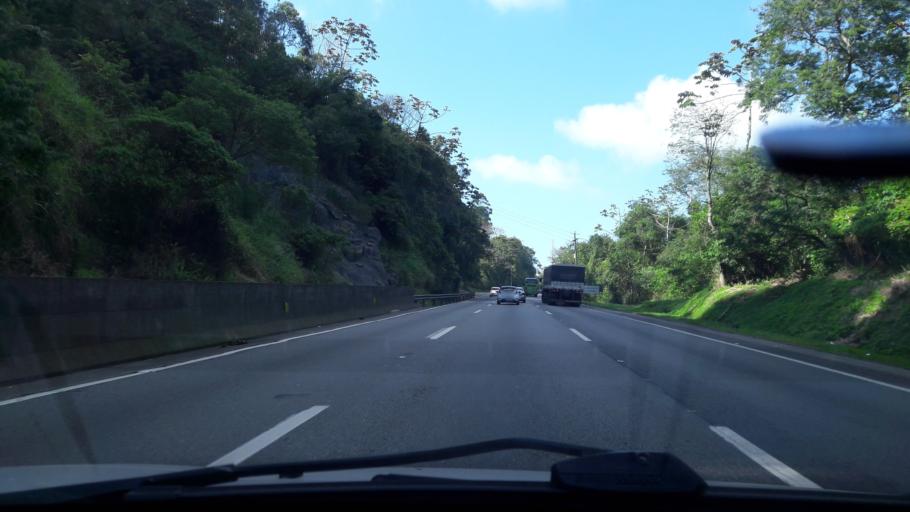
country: BR
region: Santa Catarina
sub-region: Itapema
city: Itapema
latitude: -27.0386
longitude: -48.6004
